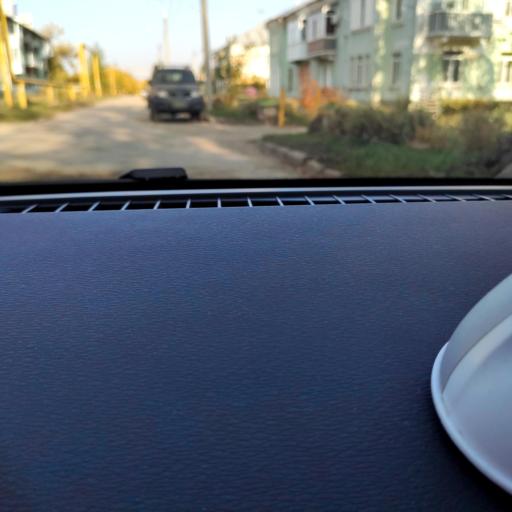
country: RU
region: Samara
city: Samara
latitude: 53.2660
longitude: 50.2386
